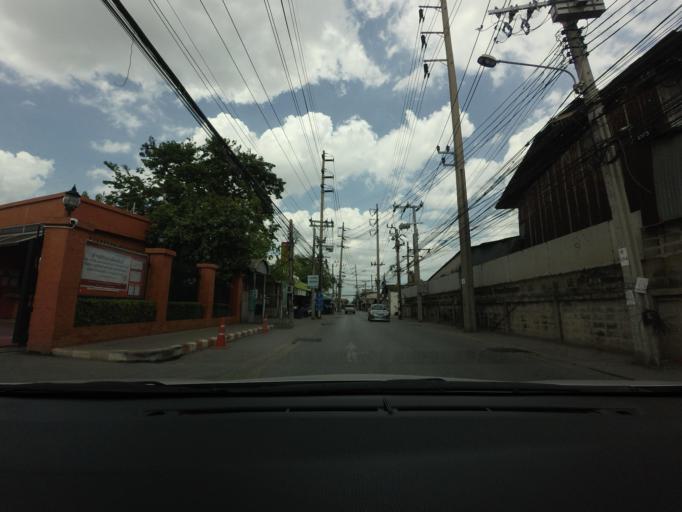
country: TH
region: Samut Prakan
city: Phra Samut Chedi
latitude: 13.6377
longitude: 100.5739
